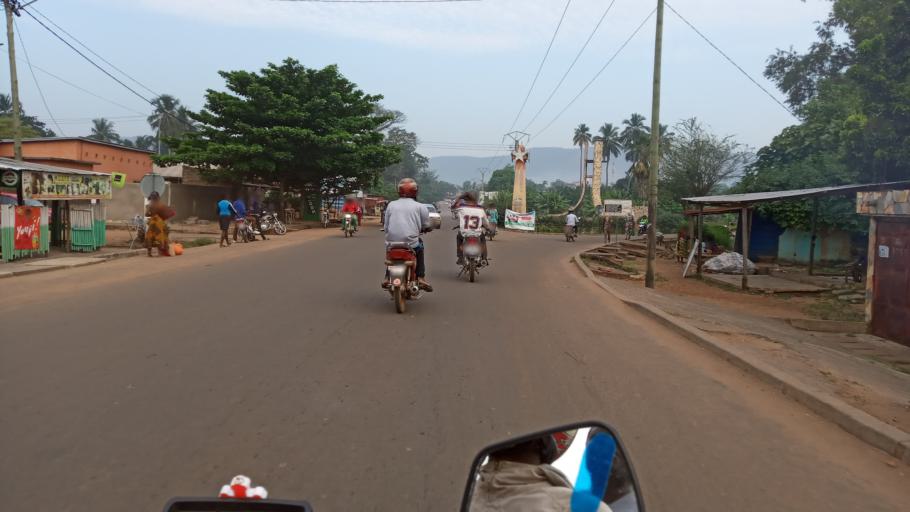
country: TG
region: Plateaux
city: Kpalime
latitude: 6.9011
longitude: 0.6342
